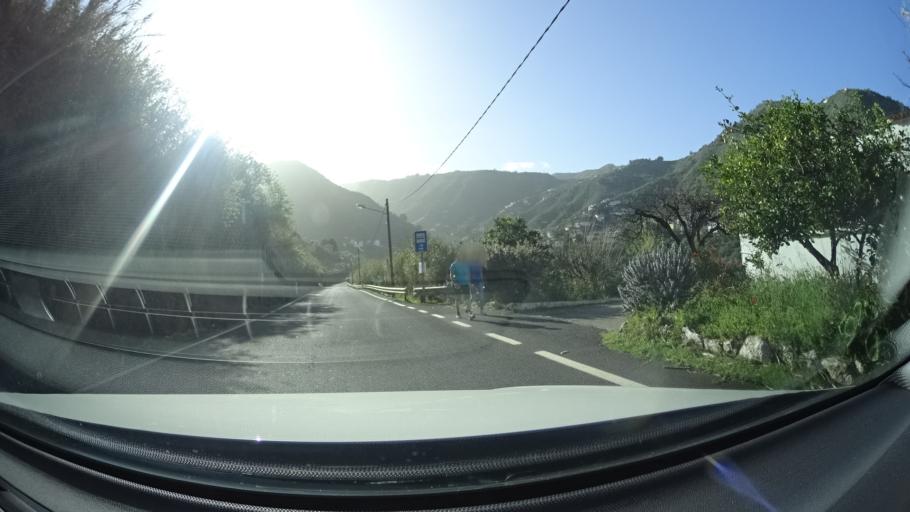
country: ES
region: Canary Islands
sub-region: Provincia de Las Palmas
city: Vega de San Mateo
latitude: 28.0173
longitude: -15.5494
